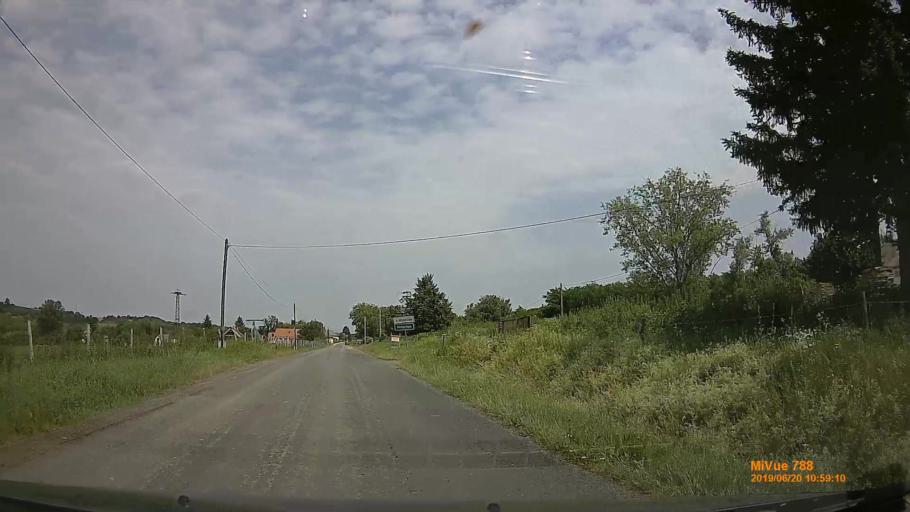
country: HU
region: Baranya
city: Mecseknadasd
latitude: 46.1660
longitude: 18.5143
